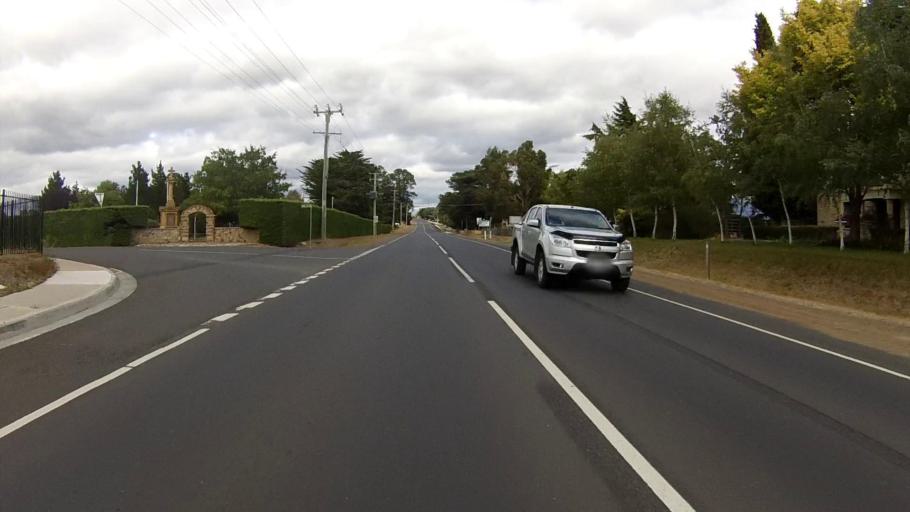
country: AU
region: Tasmania
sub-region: Brighton
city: Bridgewater
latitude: -42.6863
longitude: 147.2650
